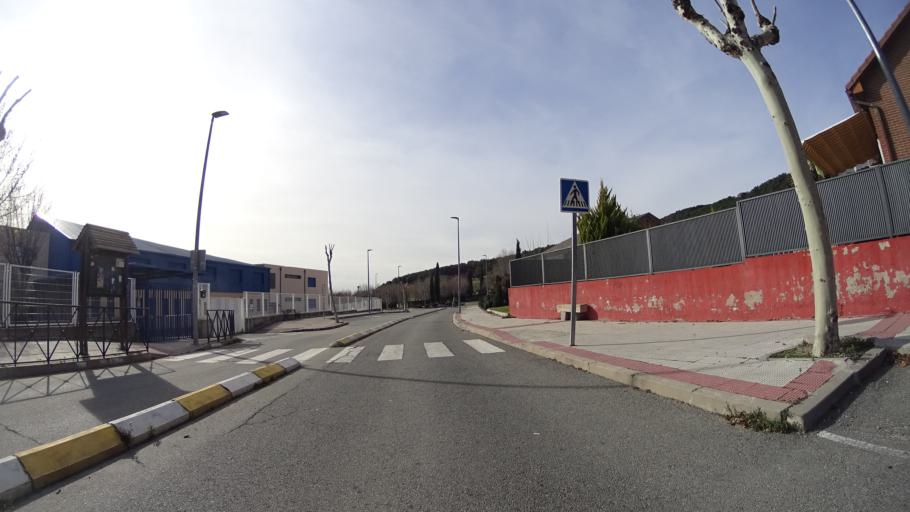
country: ES
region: Madrid
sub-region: Provincia de Madrid
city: Moralzarzal
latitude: 40.6755
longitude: -3.9765
